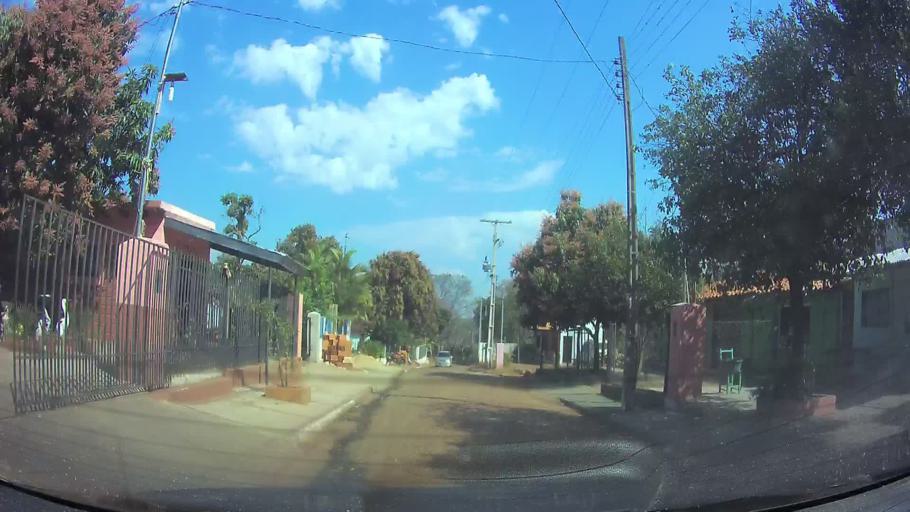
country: PY
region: Central
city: Limpio
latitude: -25.2317
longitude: -57.4401
